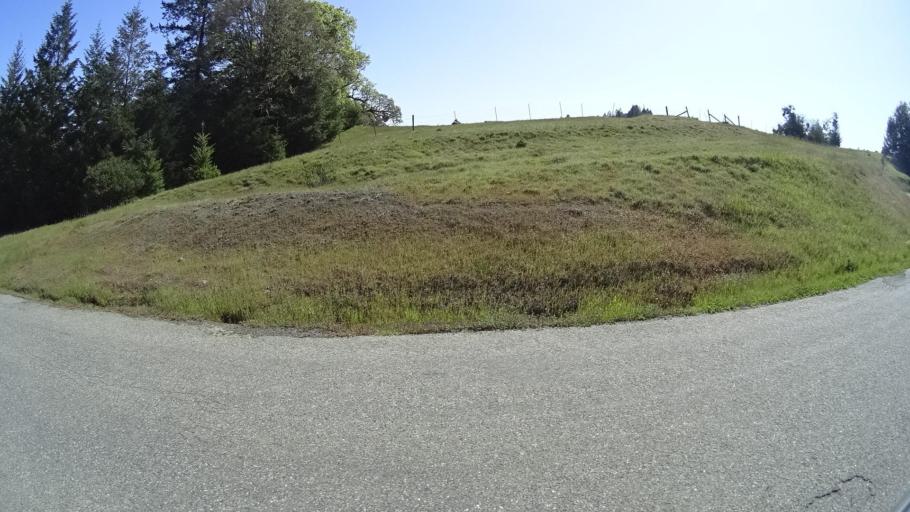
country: US
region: California
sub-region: Humboldt County
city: Redway
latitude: 40.0618
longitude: -123.6426
